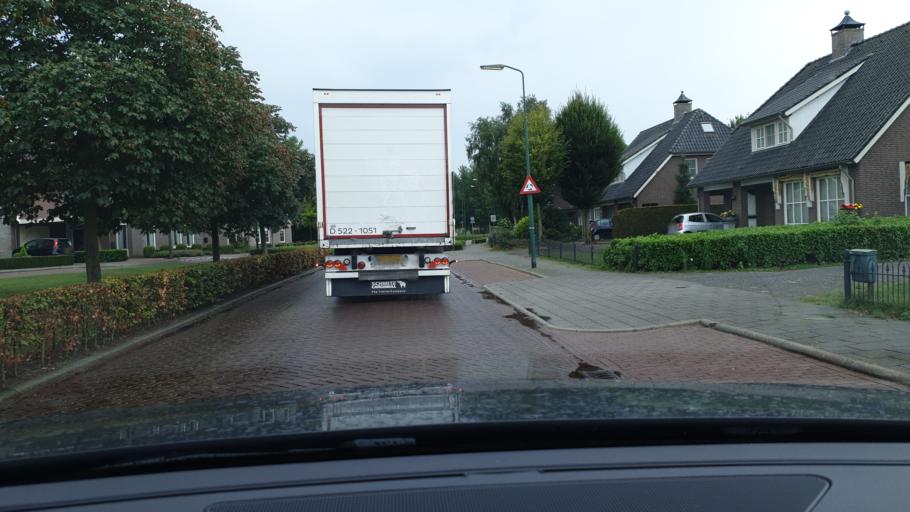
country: NL
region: North Brabant
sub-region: Gemeente Sint-Oedenrode
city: Sint-Oedenrode
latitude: 51.5579
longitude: 5.4487
